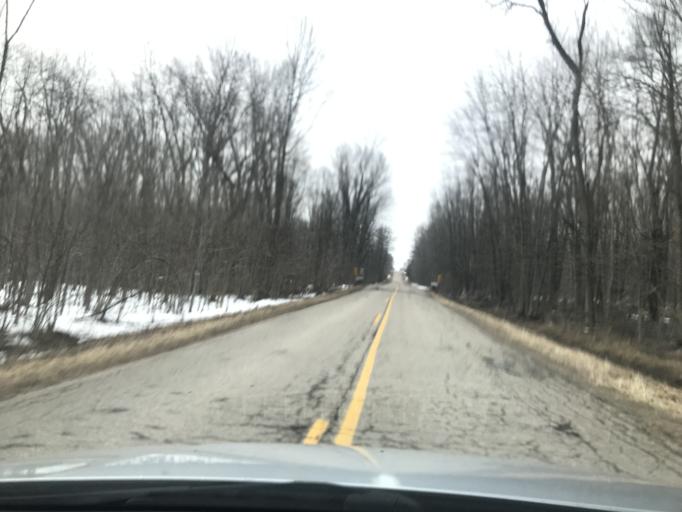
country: US
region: Wisconsin
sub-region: Oconto County
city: Oconto Falls
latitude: 44.8361
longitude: -88.1679
